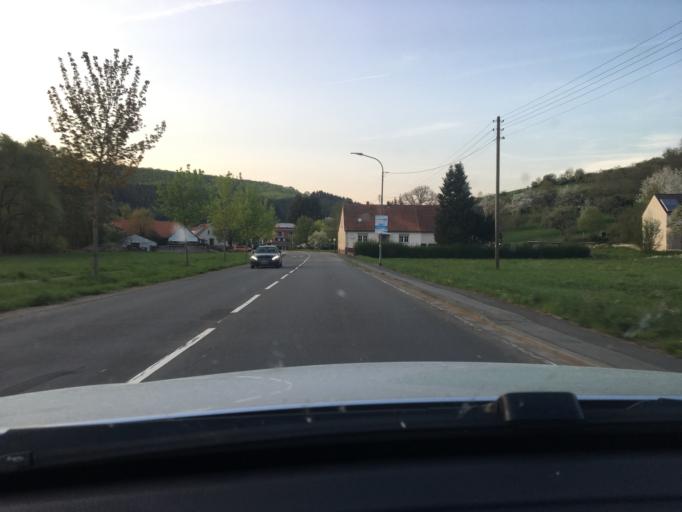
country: DE
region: Rheinland-Pfalz
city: Bayerfeld-Steckweiler
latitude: 49.6934
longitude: 7.8040
